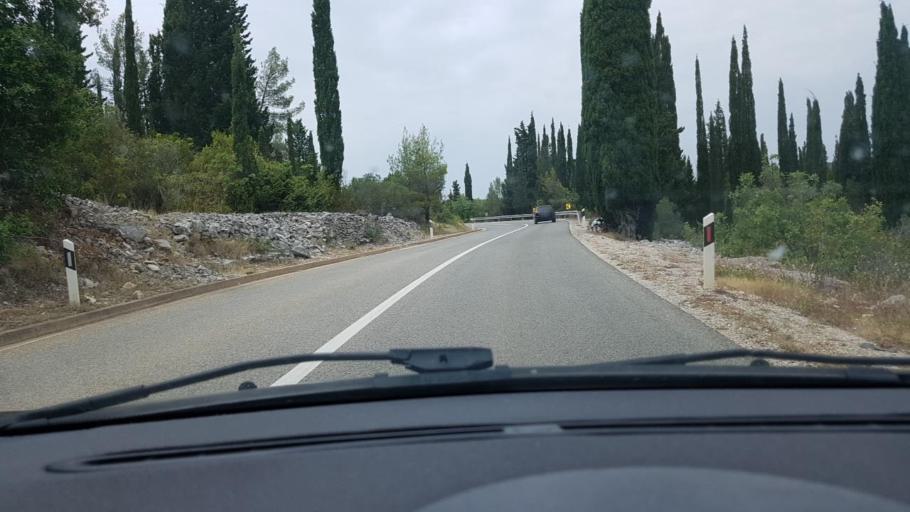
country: HR
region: Dubrovacko-Neretvanska
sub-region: Grad Korcula
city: Zrnovo
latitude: 42.9381
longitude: 17.0916
